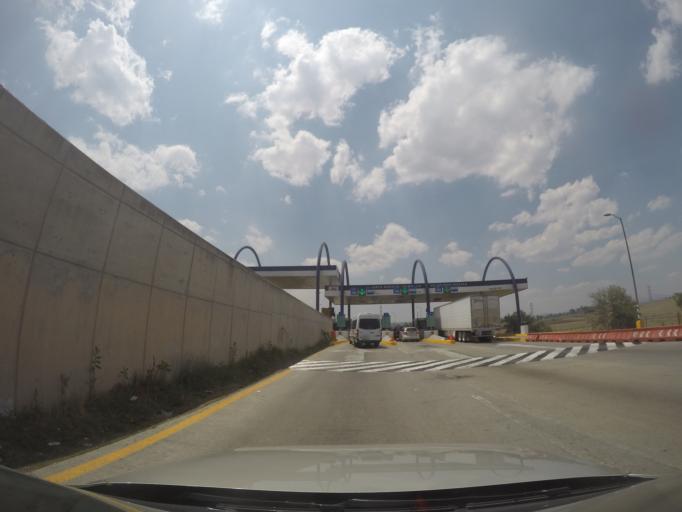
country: MX
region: Mexico
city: San Francisco Soyaniquilpan
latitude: 20.0005
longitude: -99.4896
